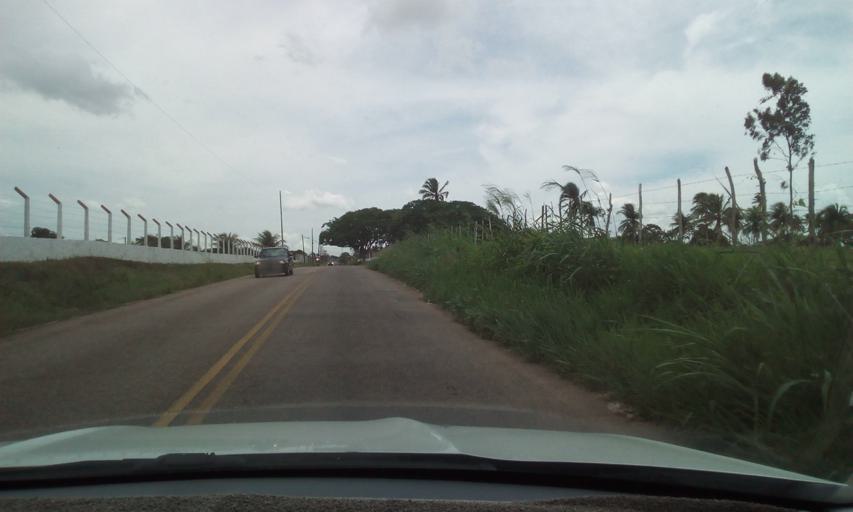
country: BR
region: Paraiba
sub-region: Mari
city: Mari
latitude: -7.0742
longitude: -35.3211
